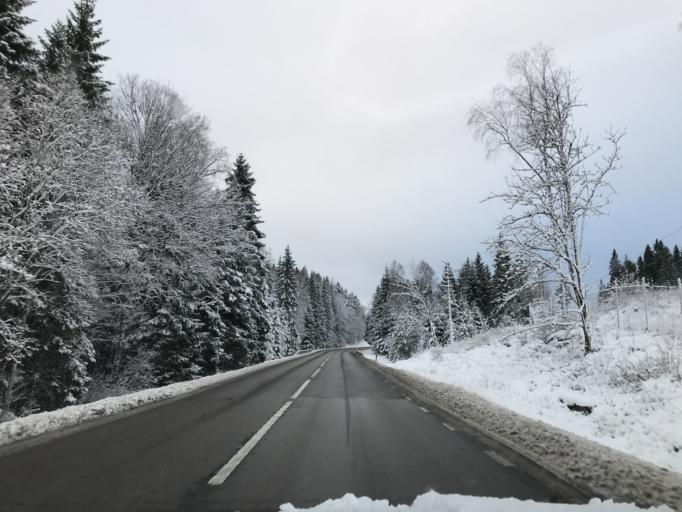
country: SE
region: Vaestra Goetaland
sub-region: Boras Kommun
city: Sandared
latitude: 57.7864
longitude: 12.7758
